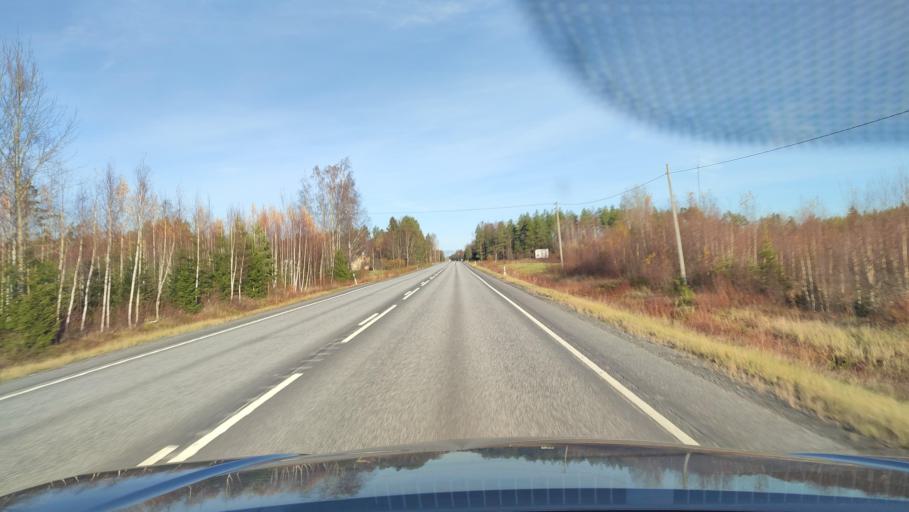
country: FI
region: Ostrobothnia
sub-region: Vaasa
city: Malax
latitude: 62.7692
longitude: 21.6566
